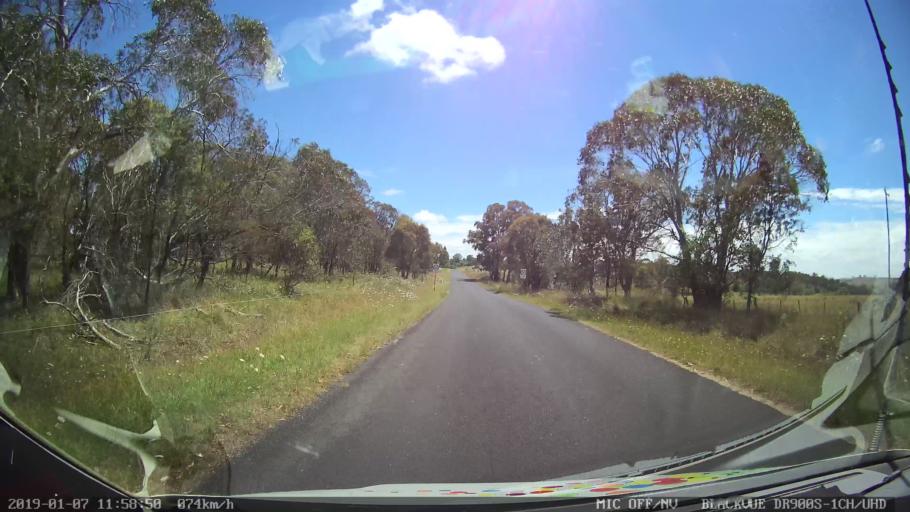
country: AU
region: New South Wales
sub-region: Guyra
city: Guyra
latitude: -30.2489
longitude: 151.6686
